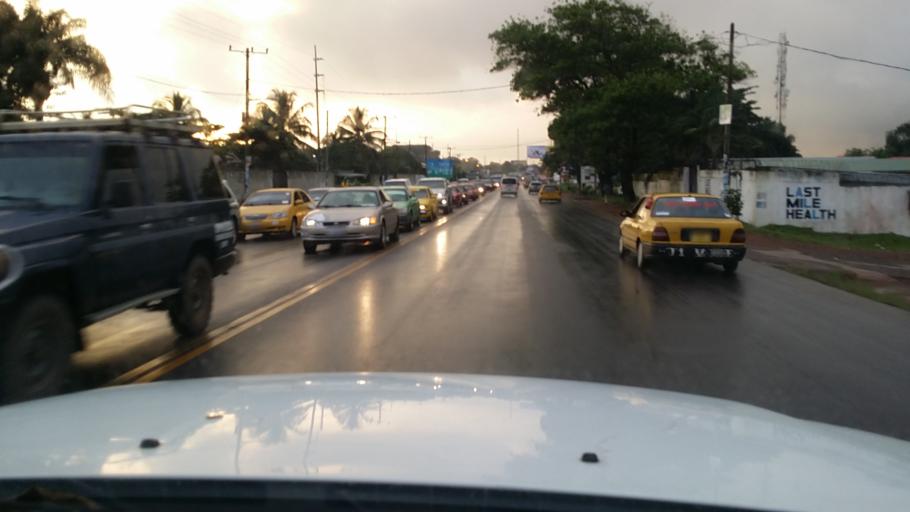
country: LR
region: Montserrado
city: Monrovia
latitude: 6.2713
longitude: -10.7395
